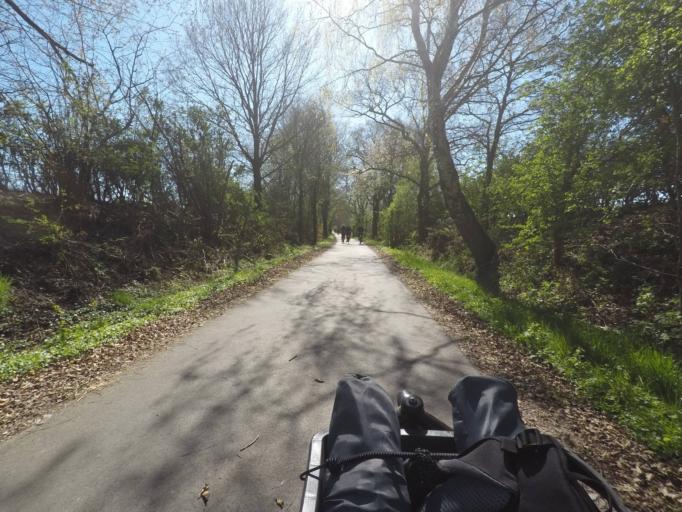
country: DE
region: Schleswig-Holstein
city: Braak
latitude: 53.6039
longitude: 10.2777
